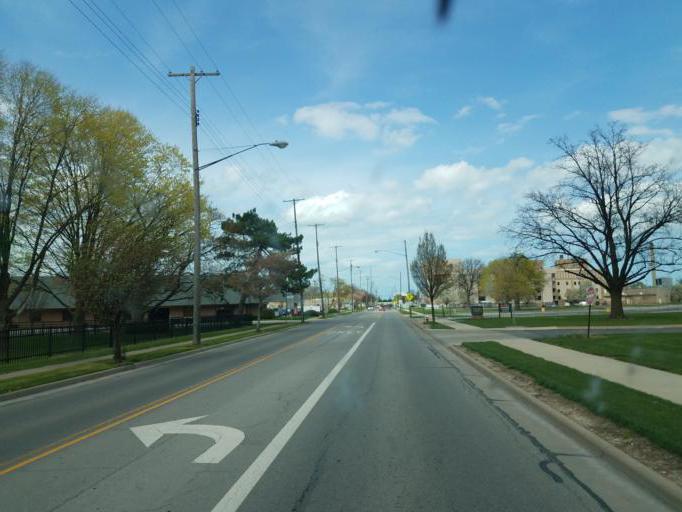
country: US
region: Ohio
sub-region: Erie County
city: Sandusky
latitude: 41.4349
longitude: -82.7141
